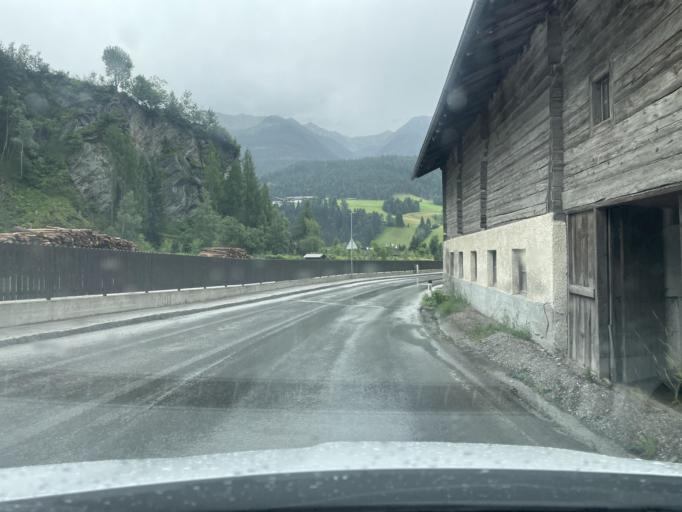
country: AT
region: Tyrol
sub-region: Politischer Bezirk Lienz
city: Heinfels
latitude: 46.7523
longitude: 12.4376
